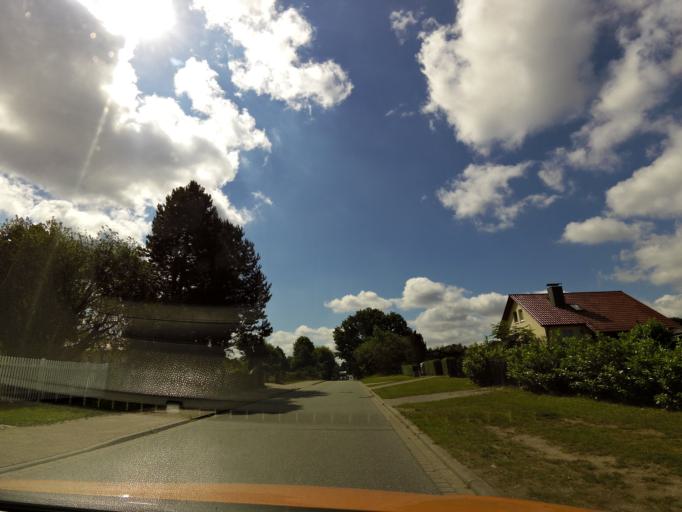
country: DE
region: Mecklenburg-Vorpommern
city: Plau am See
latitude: 53.4461
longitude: 12.2827
